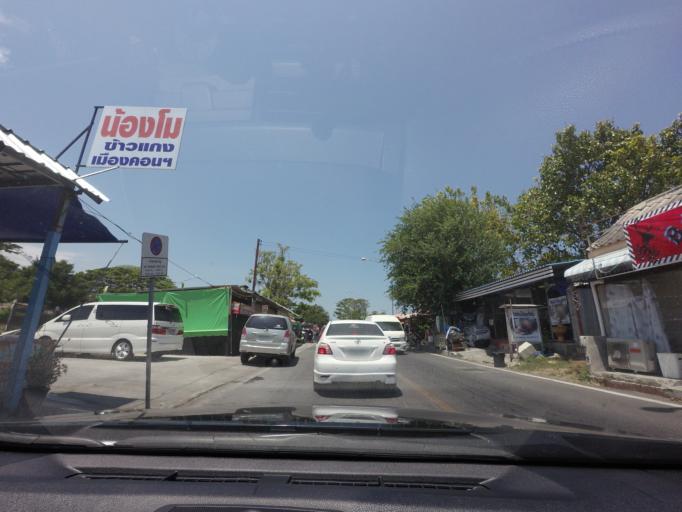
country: TH
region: Prachuap Khiri Khan
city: Hua Hin
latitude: 12.5621
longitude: 99.9561
